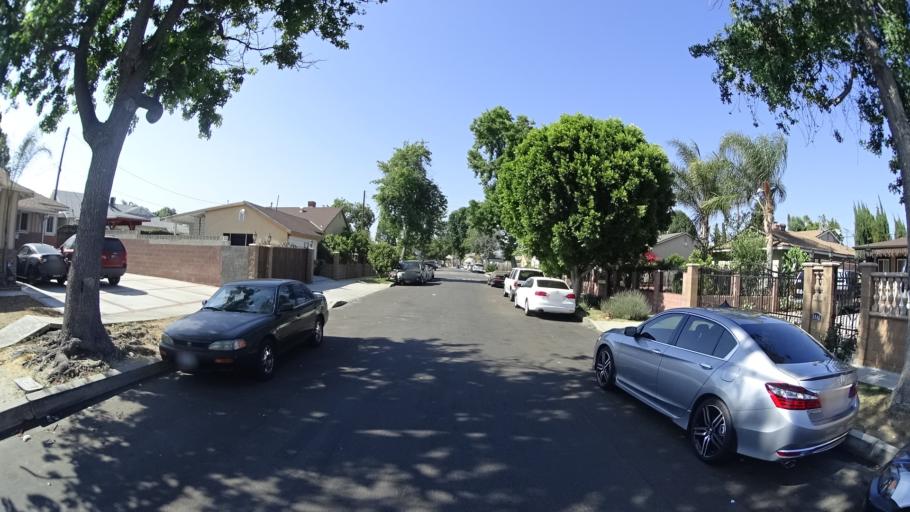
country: US
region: California
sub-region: Los Angeles County
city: Van Nuys
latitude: 34.1971
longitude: -118.4236
